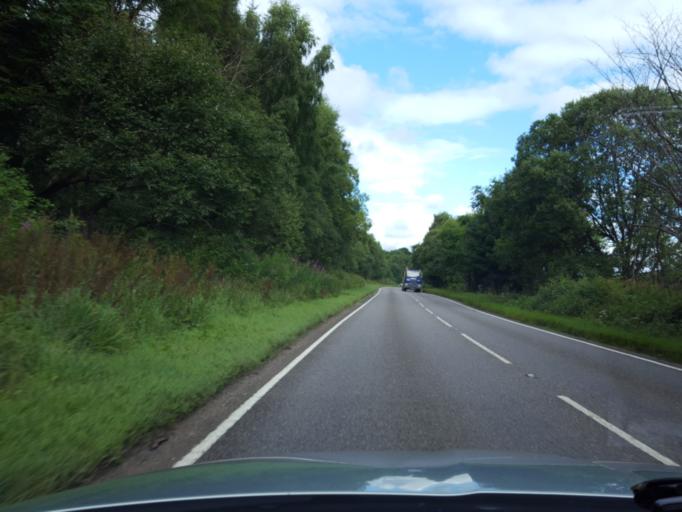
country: GB
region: Scotland
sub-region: Moray
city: Rothes
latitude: 57.5059
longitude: -3.1975
